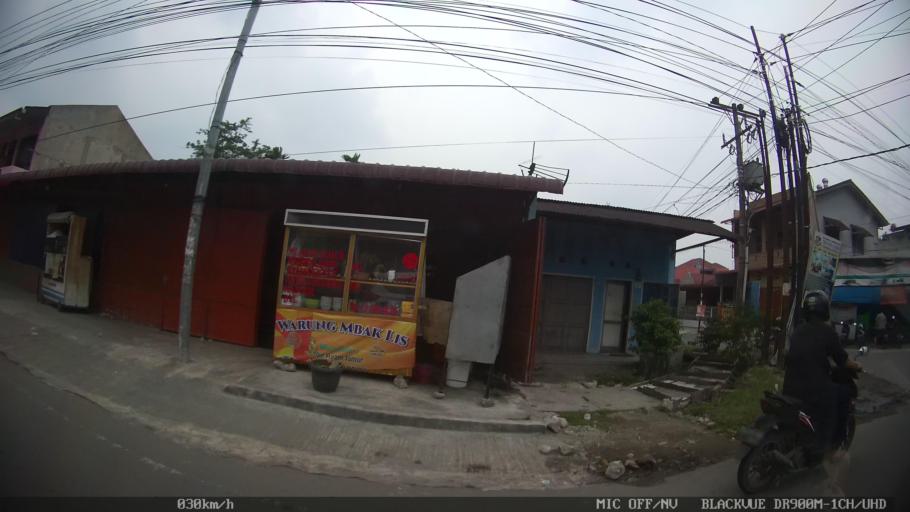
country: ID
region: North Sumatra
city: Medan
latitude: 3.5603
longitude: 98.7029
